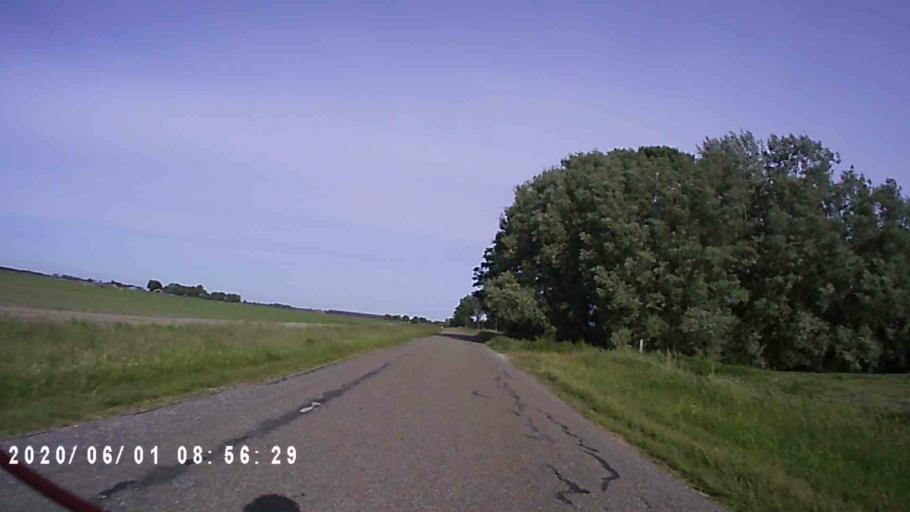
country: NL
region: Friesland
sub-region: Gemeente Leeuwarderadeel
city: Britsum
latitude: 53.2795
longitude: 5.8187
